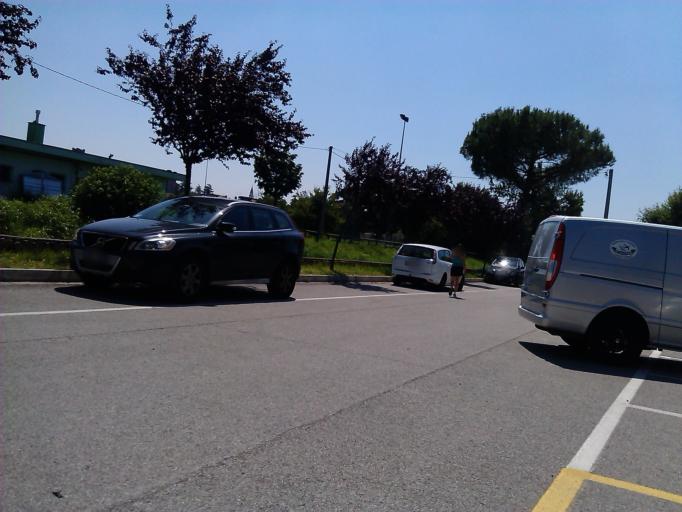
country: IT
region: Veneto
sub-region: Provincia di Treviso
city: Castelfranco Veneto
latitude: 45.6719
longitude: 11.9185
